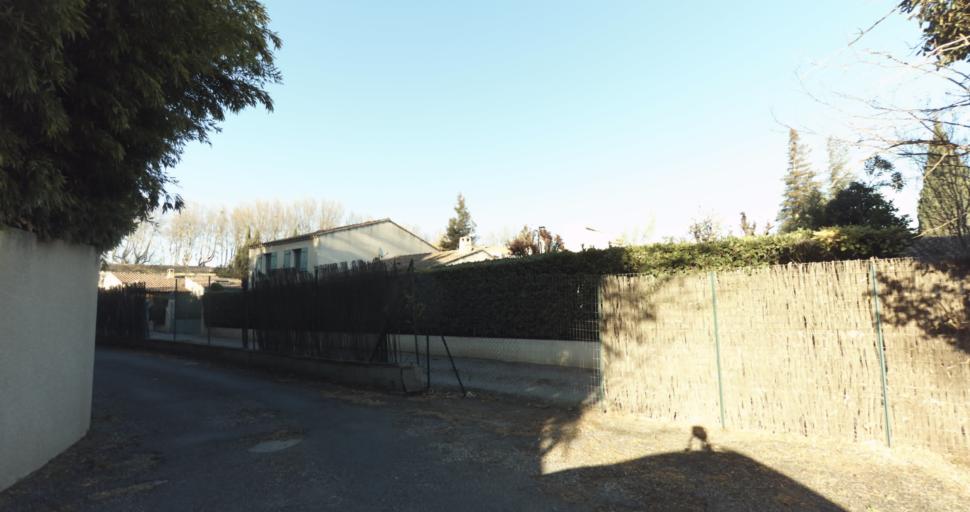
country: FR
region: Provence-Alpes-Cote d'Azur
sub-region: Departement des Bouches-du-Rhone
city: Pelissanne
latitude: 43.6309
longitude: 5.1443
